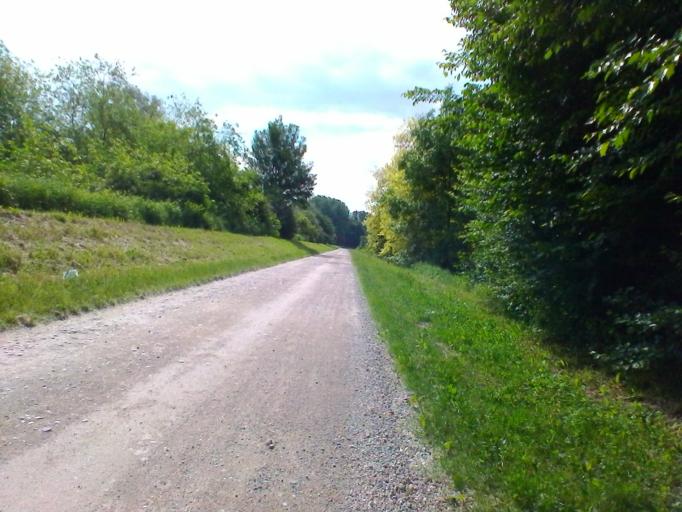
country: IT
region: Lombardy
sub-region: Provincia di Mantova
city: Cerese
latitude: 45.1349
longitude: 10.8063
